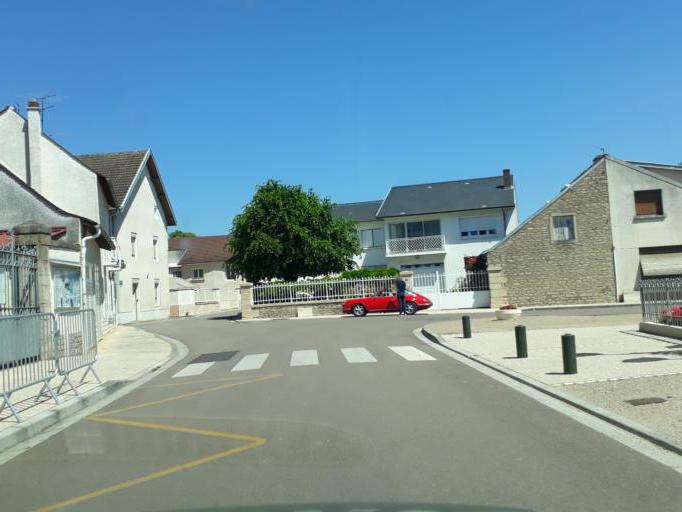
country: FR
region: Bourgogne
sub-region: Departement de la Cote-d'Or
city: Nuits-Saint-Georges
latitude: 47.1653
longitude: 4.9800
